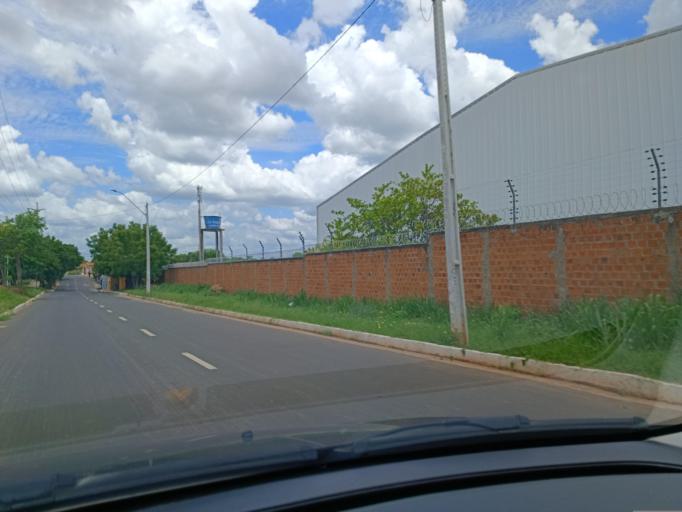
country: BR
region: Piaui
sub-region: Teresina
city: Teresina
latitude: -5.0681
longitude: -42.7514
